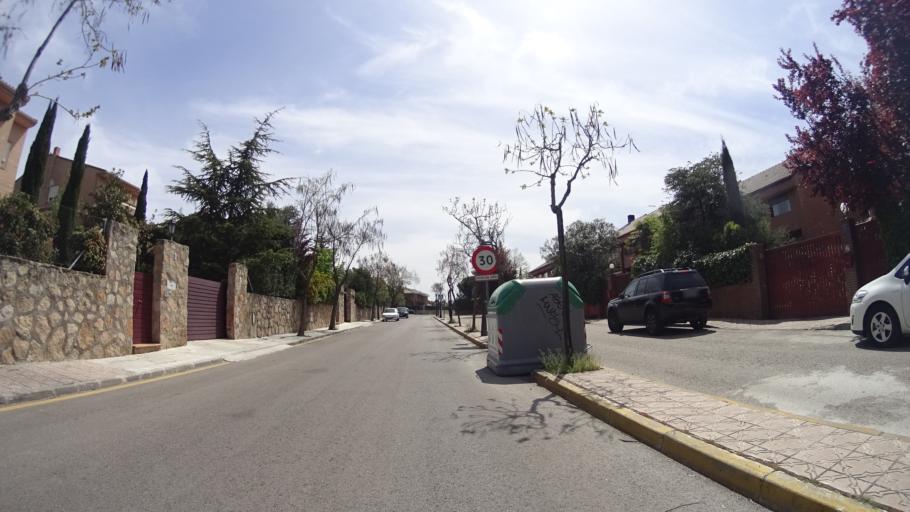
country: ES
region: Madrid
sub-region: Provincia de Madrid
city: Torrelodones
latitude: 40.5807
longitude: -3.9492
